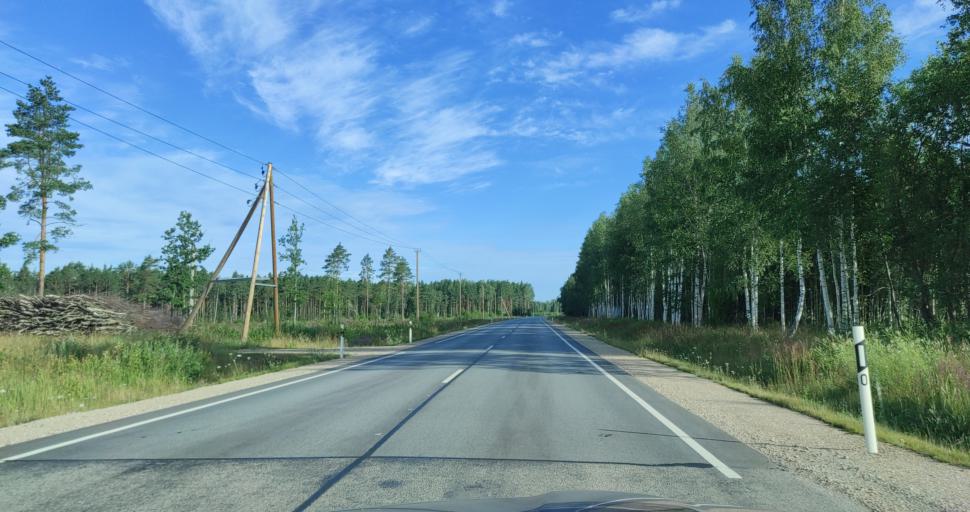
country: LV
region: Pavilostas
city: Pavilosta
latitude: 56.7997
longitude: 21.2307
